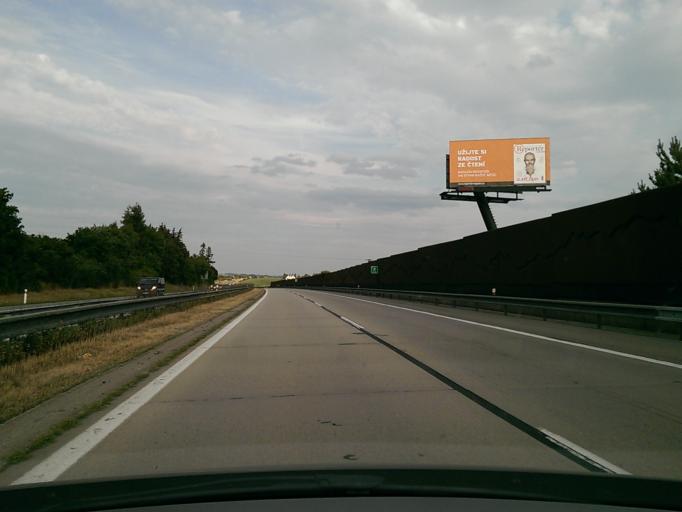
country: CZ
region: Vysocina
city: Merin
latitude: 49.3920
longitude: 15.8998
